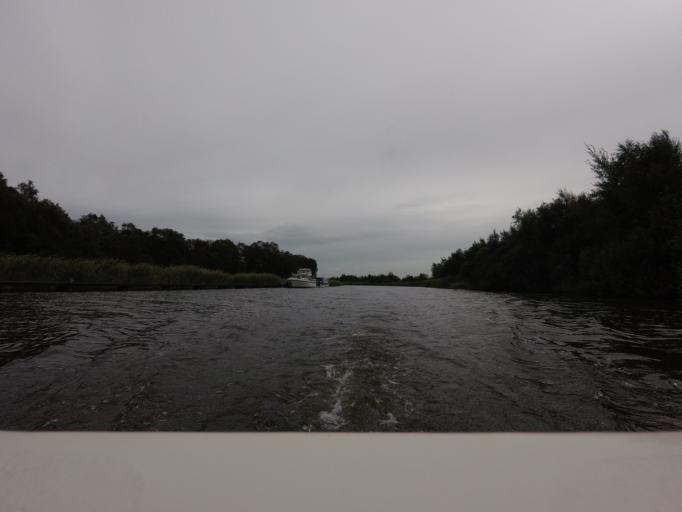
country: NL
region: Friesland
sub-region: Gemeente Boarnsterhim
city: Warten
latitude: 53.1121
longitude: 5.8817
